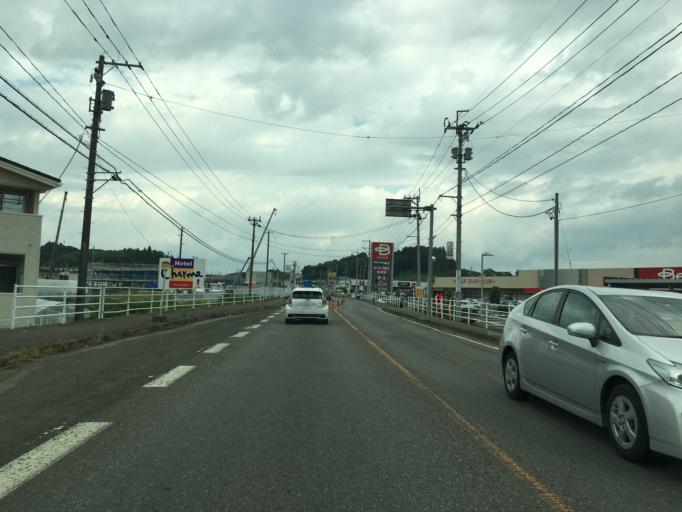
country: JP
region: Fukushima
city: Nihommatsu
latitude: 37.6119
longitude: 140.4614
